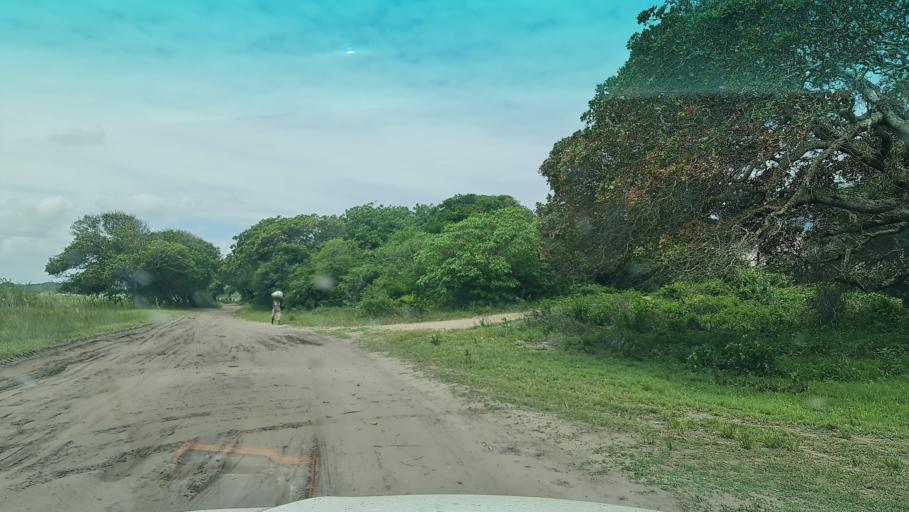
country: MZ
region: Maputo
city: Manhica
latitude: -25.5238
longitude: 32.8604
